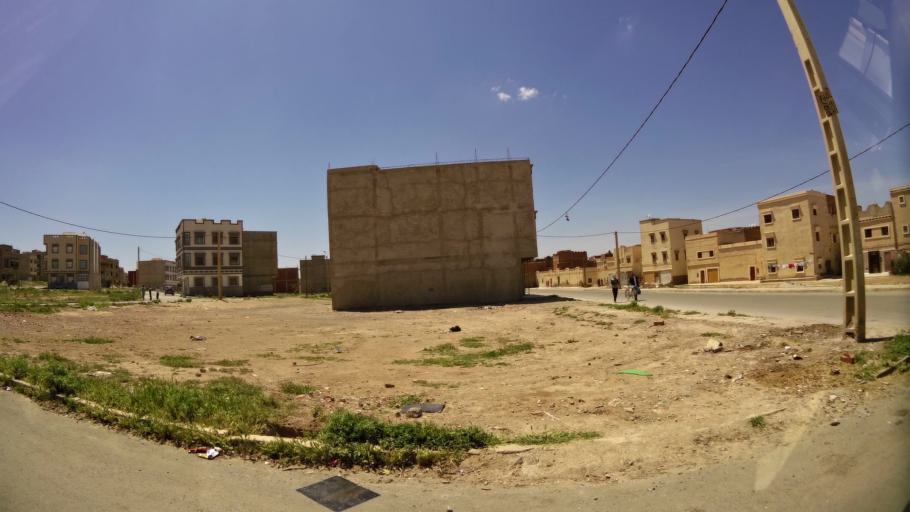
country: MA
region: Oriental
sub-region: Oujda-Angad
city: Oujda
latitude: 34.6554
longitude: -1.9203
